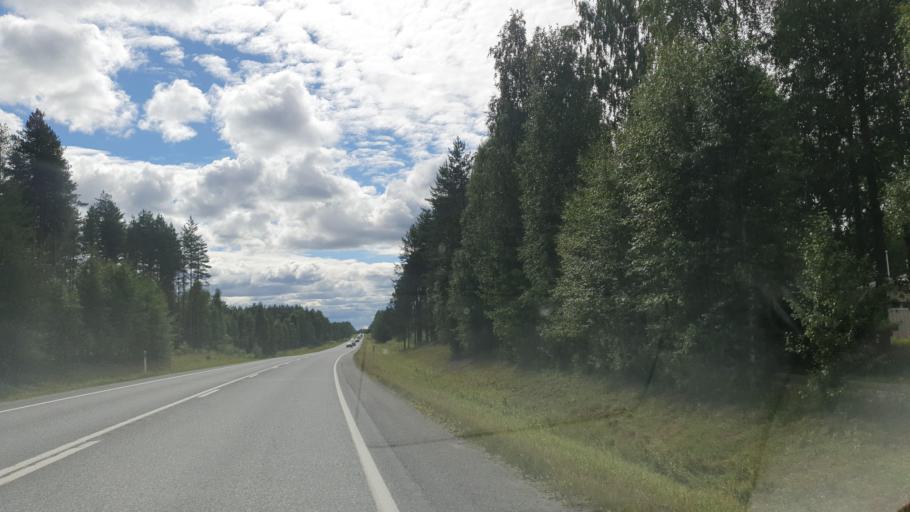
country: FI
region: Kainuu
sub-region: Kajaani
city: Kajaani
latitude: 64.1375
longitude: 27.4933
